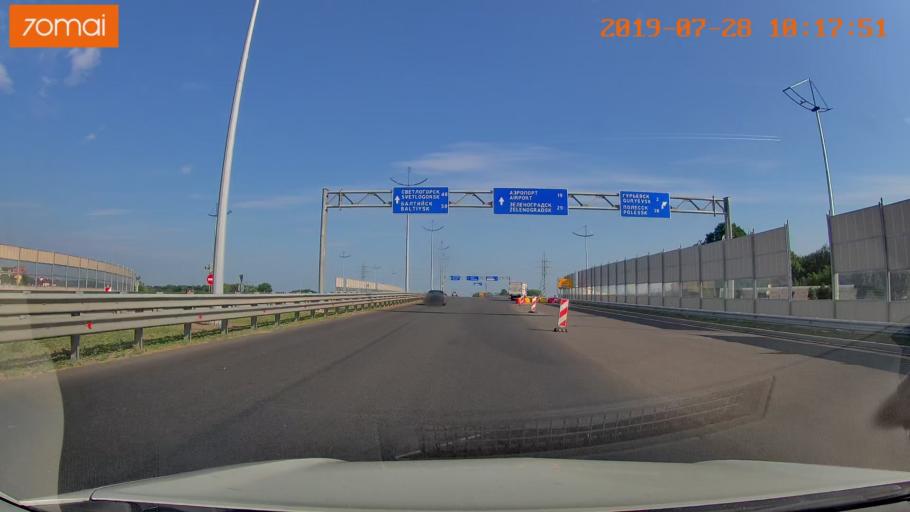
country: RU
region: Kaliningrad
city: Maloye Isakovo
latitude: 54.7443
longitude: 20.5924
